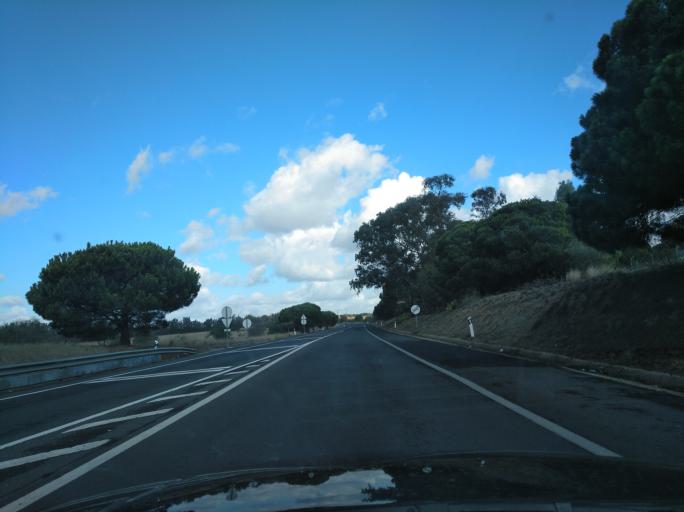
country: PT
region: Faro
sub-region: Vila Real de Santo Antonio
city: Monte Gordo
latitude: 37.1828
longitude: -7.4913
